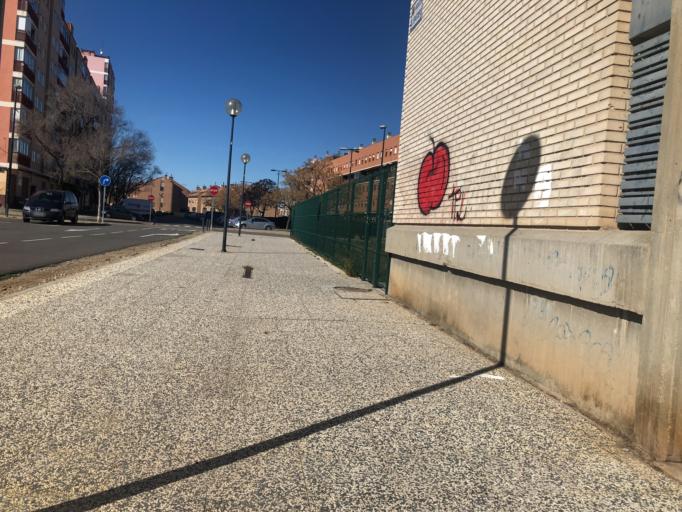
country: ES
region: Aragon
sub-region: Provincia de Zaragoza
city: Zaragoza
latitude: 41.6674
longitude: -0.8236
